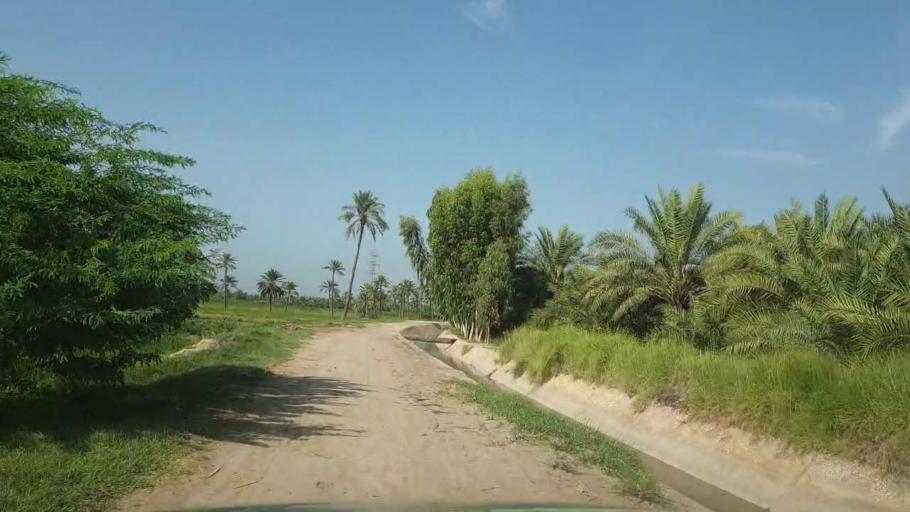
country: PK
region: Sindh
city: Rohri
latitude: 27.6572
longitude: 68.8826
